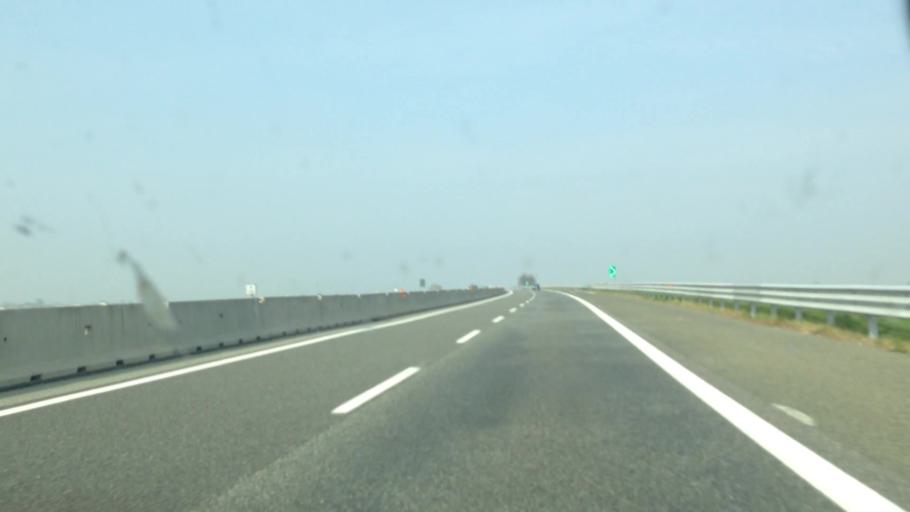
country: IT
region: Piedmont
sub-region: Provincia di Vercelli
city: Crova
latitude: 45.3422
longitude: 8.2090
